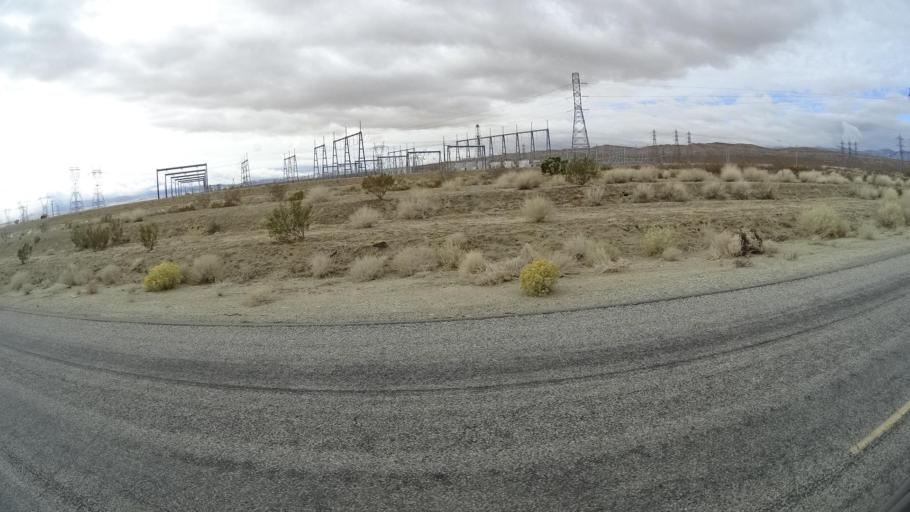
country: US
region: California
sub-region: Los Angeles County
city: Green Valley
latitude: 34.8579
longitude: -118.4323
